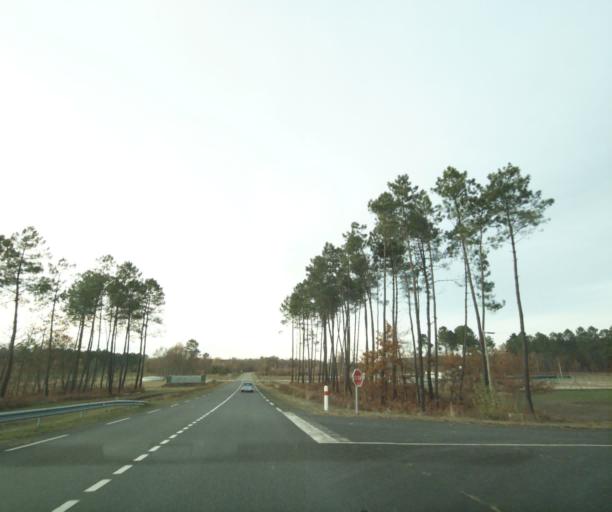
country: FR
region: Aquitaine
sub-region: Departement de la Gironde
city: Bazas
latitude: 44.2711
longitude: -0.2394
